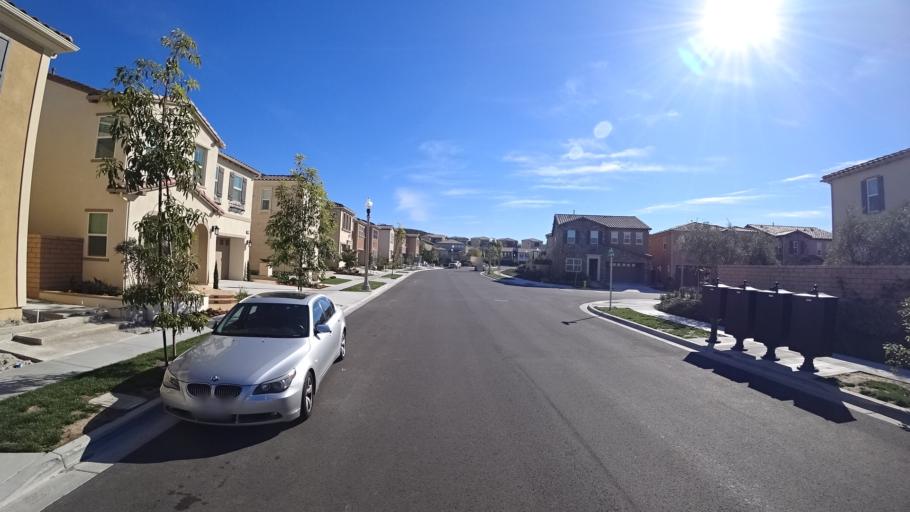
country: US
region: California
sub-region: Orange County
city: Foothill Ranch
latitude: 33.6750
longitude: -117.6796
